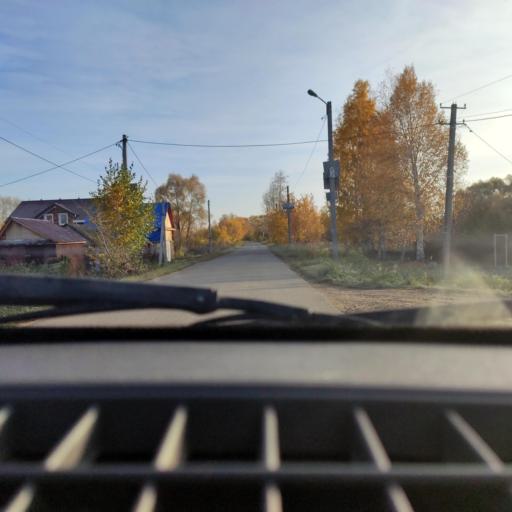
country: RU
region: Bashkortostan
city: Avdon
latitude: 54.6462
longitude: 55.7492
